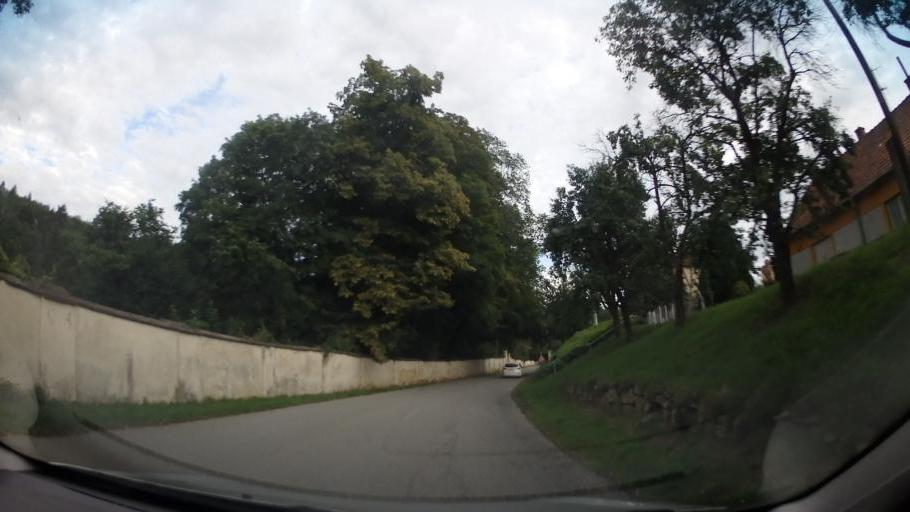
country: CZ
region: Olomoucky
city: Horni Stepanov
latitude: 49.5449
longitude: 16.7160
